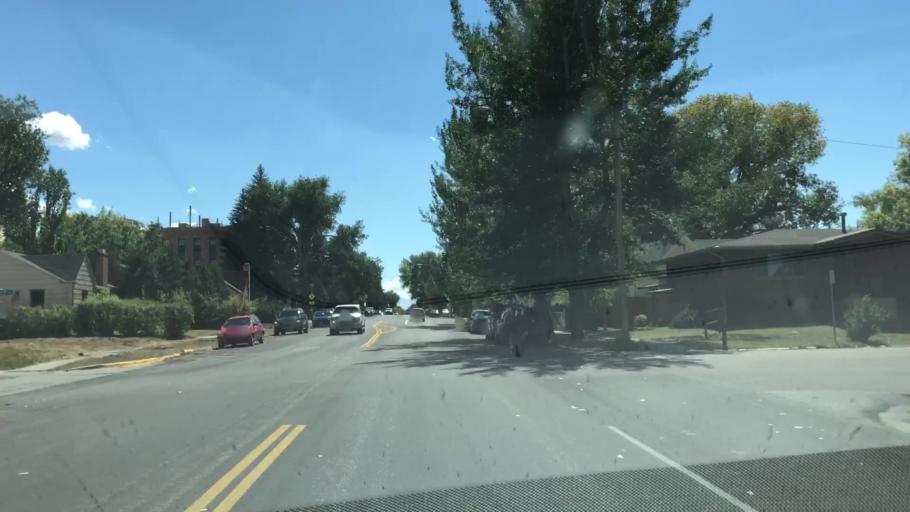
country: US
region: Wyoming
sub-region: Albany County
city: Laramie
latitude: 41.3164
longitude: -105.5851
